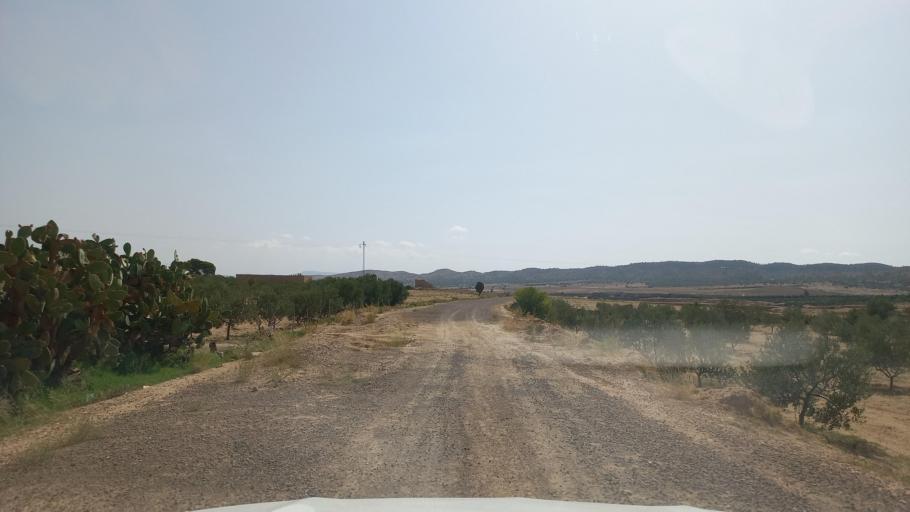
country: TN
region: Al Qasrayn
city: Sbiba
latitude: 35.3927
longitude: 8.9565
